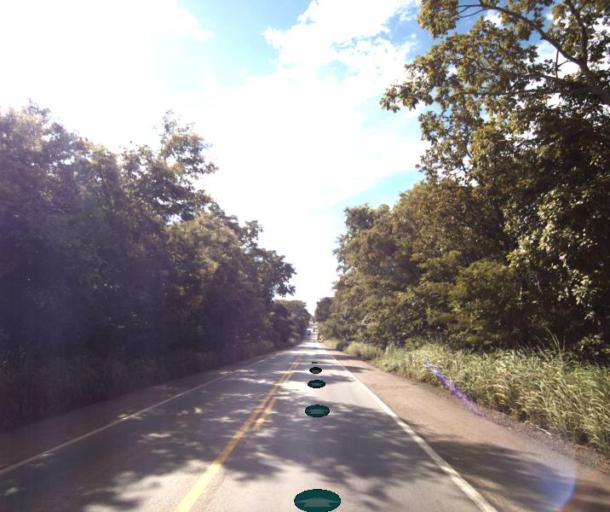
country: BR
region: Goias
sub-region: Jaragua
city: Jaragua
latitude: -15.5962
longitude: -49.4078
